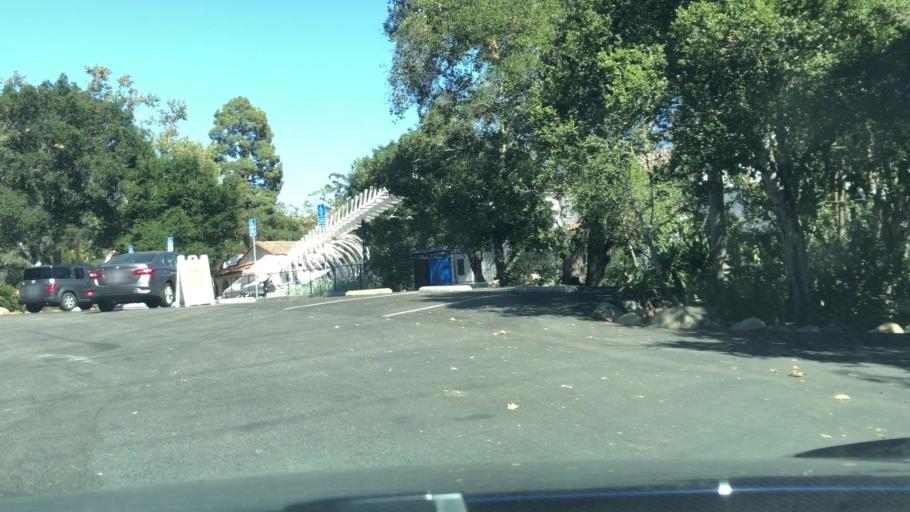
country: US
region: California
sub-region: Santa Barbara County
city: Mission Canyon
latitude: 34.4412
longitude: -119.7155
